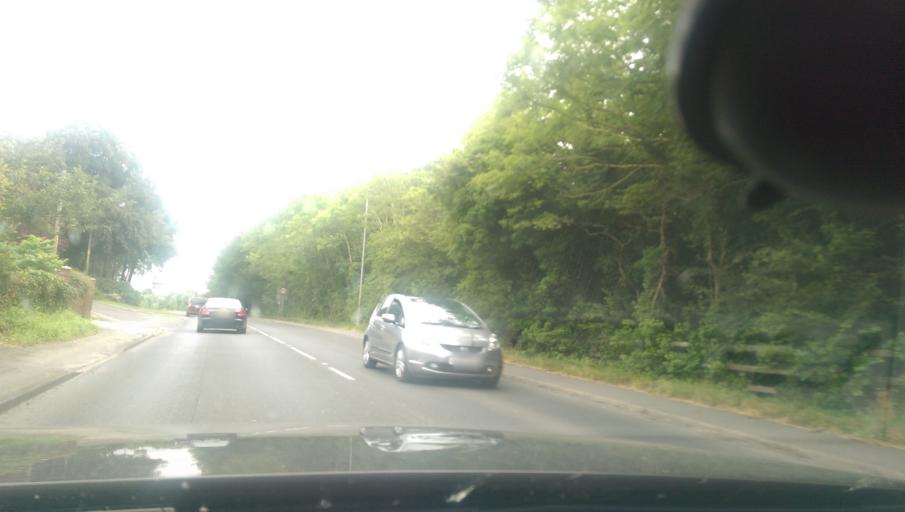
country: GB
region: England
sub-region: Wiltshire
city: Amesbury
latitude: 51.1868
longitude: -1.7833
